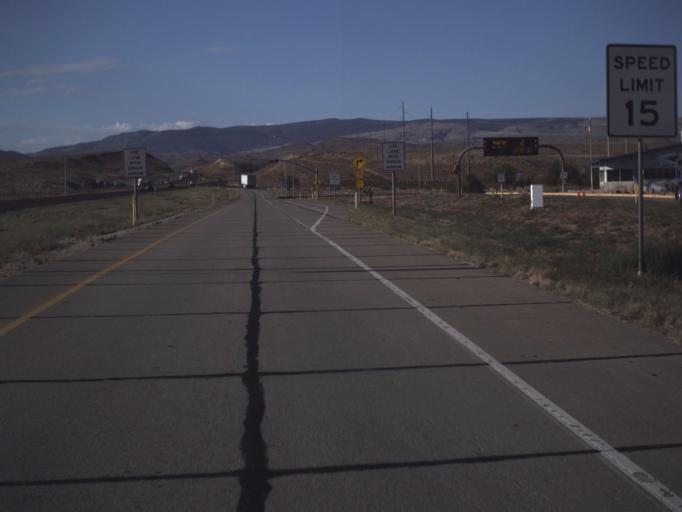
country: US
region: Utah
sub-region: Washington County
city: Saint George
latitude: 37.0133
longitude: -113.6150
